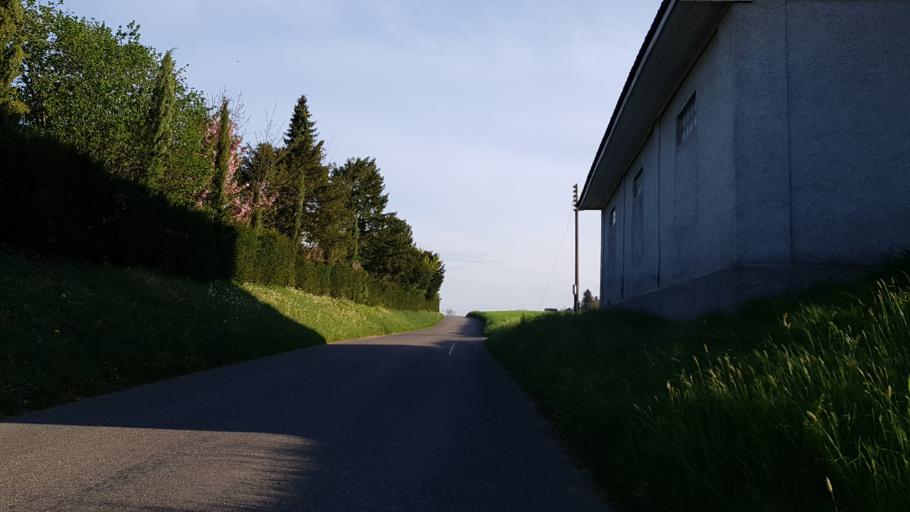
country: CH
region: Aargau
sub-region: Bezirk Kulm
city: Reinach
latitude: 47.2833
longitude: 8.1964
